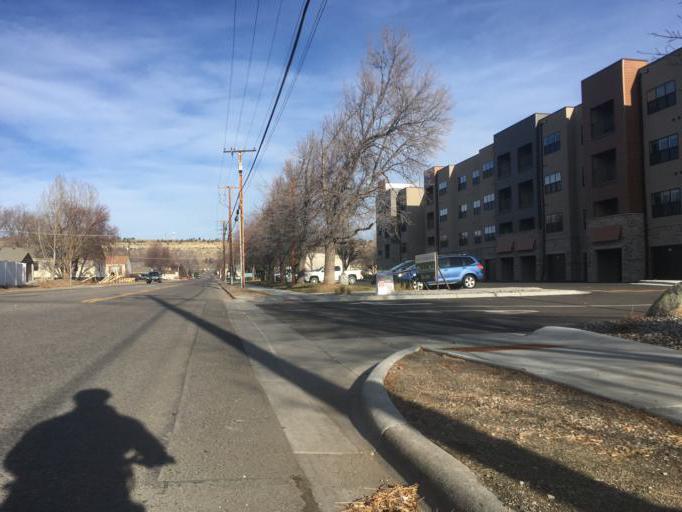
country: US
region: Montana
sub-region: Yellowstone County
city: Billings
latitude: 45.7860
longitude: -108.5589
